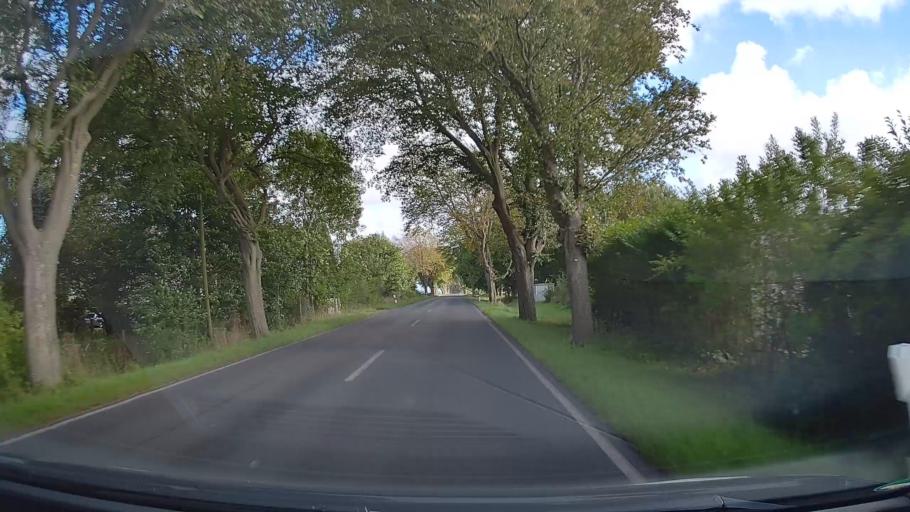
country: DE
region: Mecklenburg-Vorpommern
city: Bergen auf Ruegen
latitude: 54.4071
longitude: 13.4460
